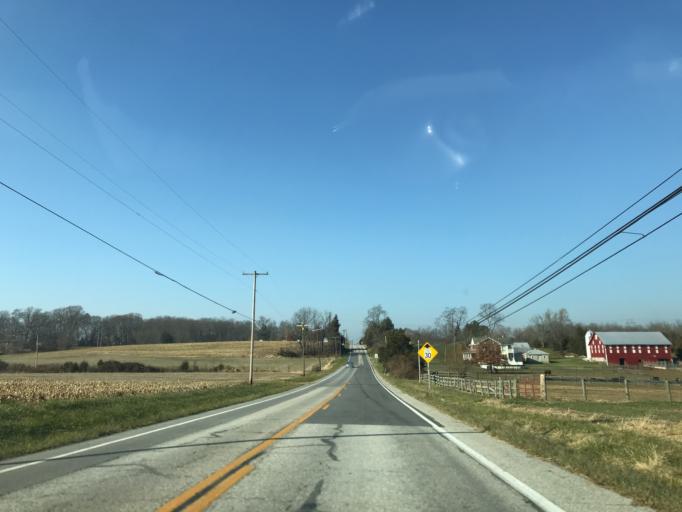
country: US
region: Maryland
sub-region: Carroll County
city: Taneytown
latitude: 39.6441
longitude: -77.1460
